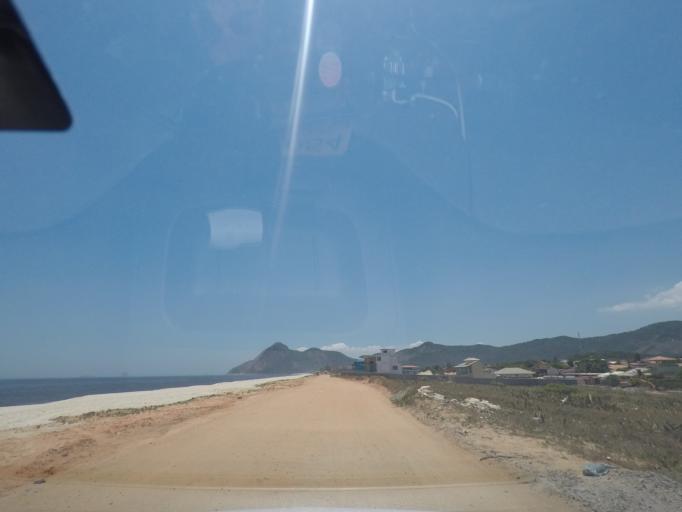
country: BR
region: Rio de Janeiro
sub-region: Niteroi
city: Niteroi
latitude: -22.9693
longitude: -42.9721
